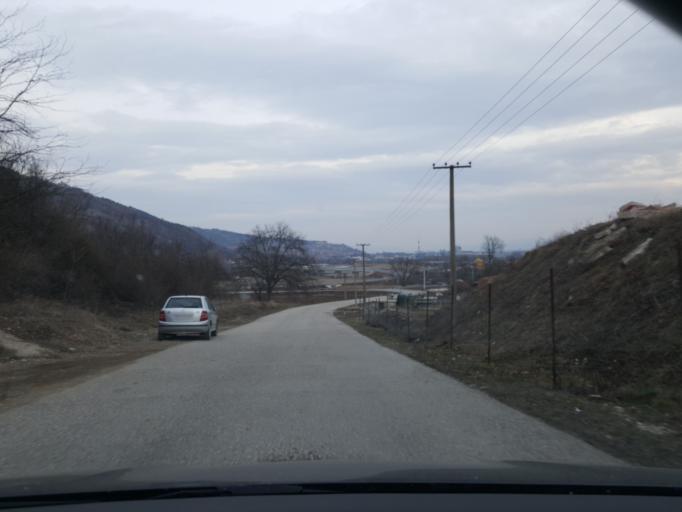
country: RS
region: Central Serbia
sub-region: Pirotski Okrug
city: Pirot
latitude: 43.1939
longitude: 22.5589
